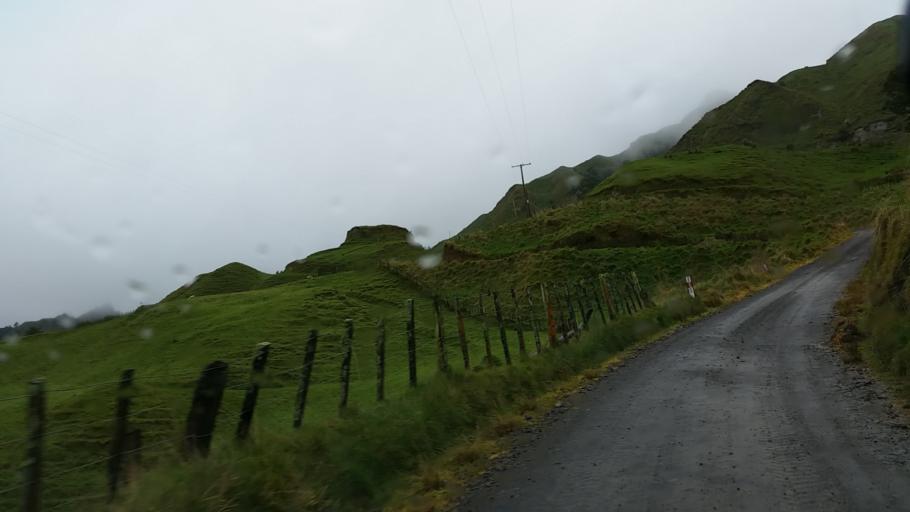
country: NZ
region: Taranaki
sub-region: South Taranaki District
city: Eltham
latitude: -39.4767
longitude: 174.4093
